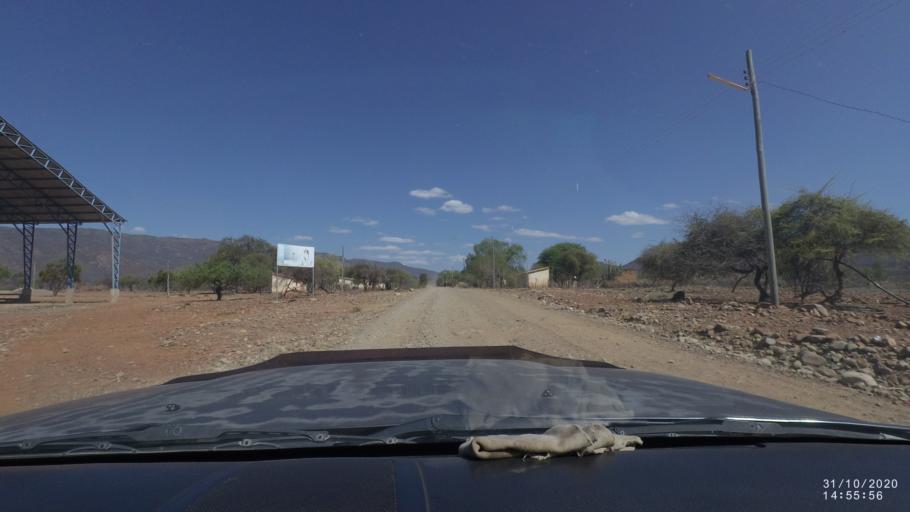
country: BO
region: Cochabamba
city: Aiquile
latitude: -18.2353
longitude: -64.8550
